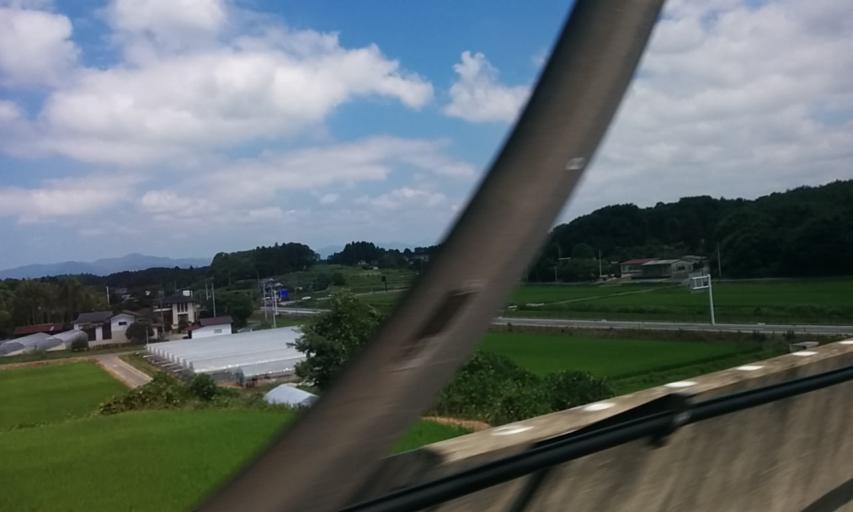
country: JP
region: Fukushima
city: Sukagawa
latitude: 37.2752
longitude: 140.3208
